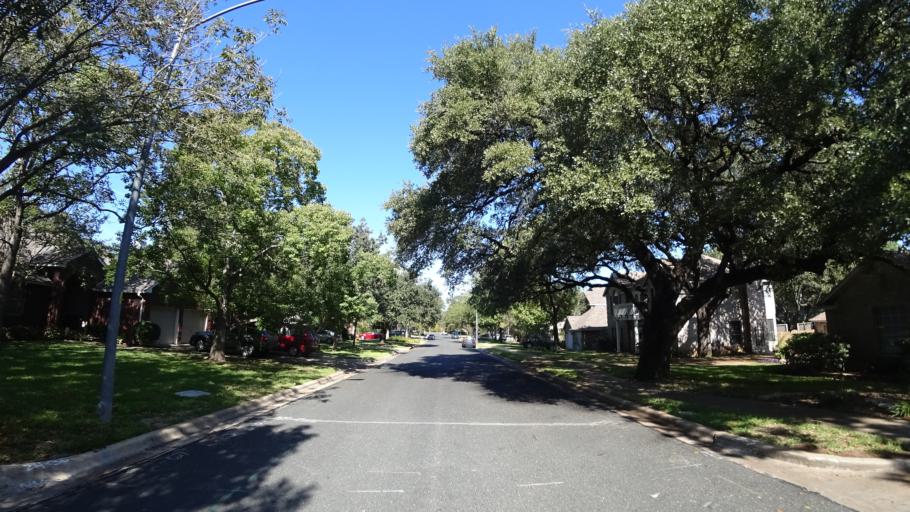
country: US
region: Texas
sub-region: Travis County
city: Shady Hollow
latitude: 30.2185
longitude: -97.8722
